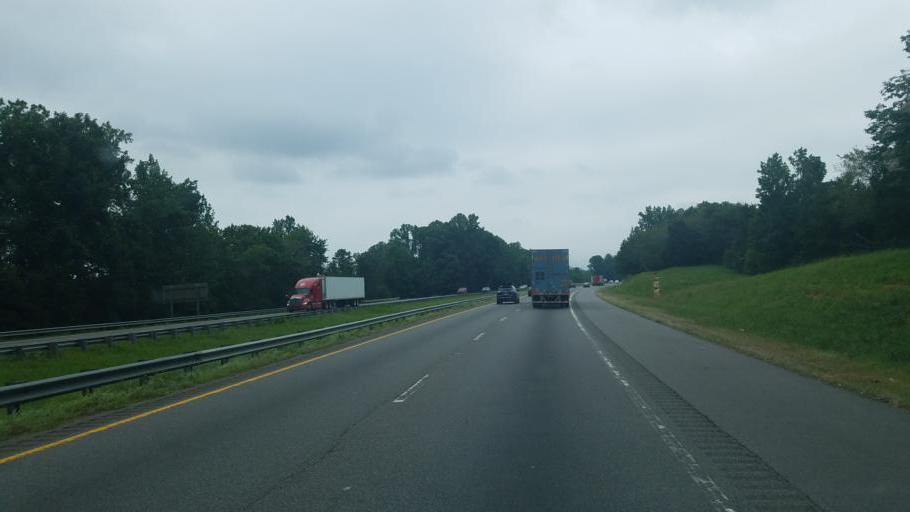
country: US
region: North Carolina
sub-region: Iredell County
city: Troutman
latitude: 35.6475
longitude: -80.8647
